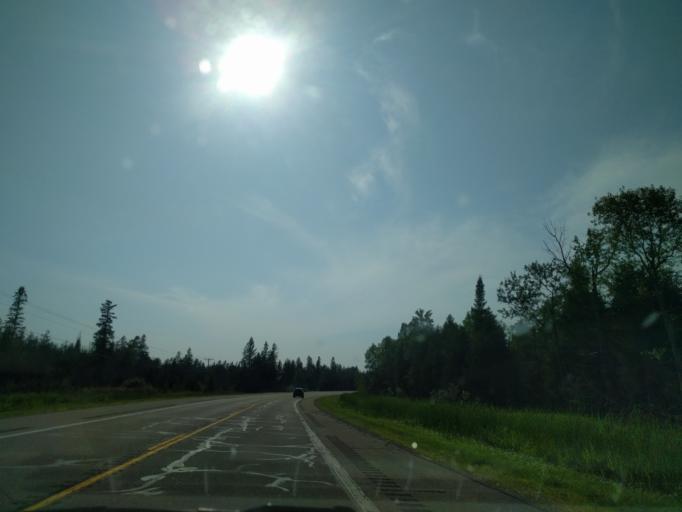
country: US
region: Michigan
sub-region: Delta County
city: Gladstone
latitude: 45.9783
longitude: -87.0963
